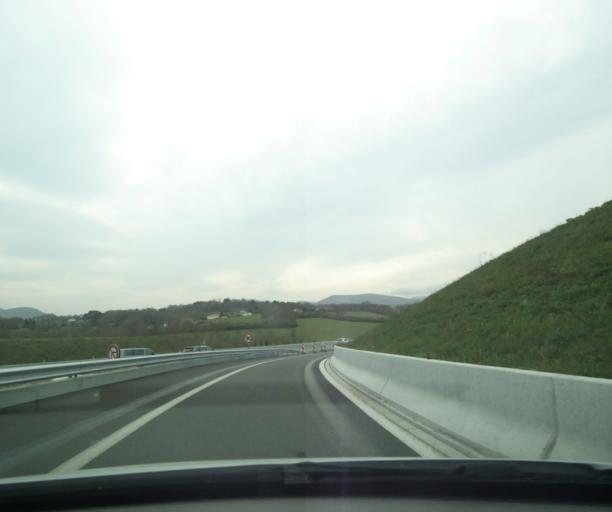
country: FR
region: Aquitaine
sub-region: Departement des Pyrenees-Atlantiques
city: Ciboure
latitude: 43.3716
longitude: -1.6788
